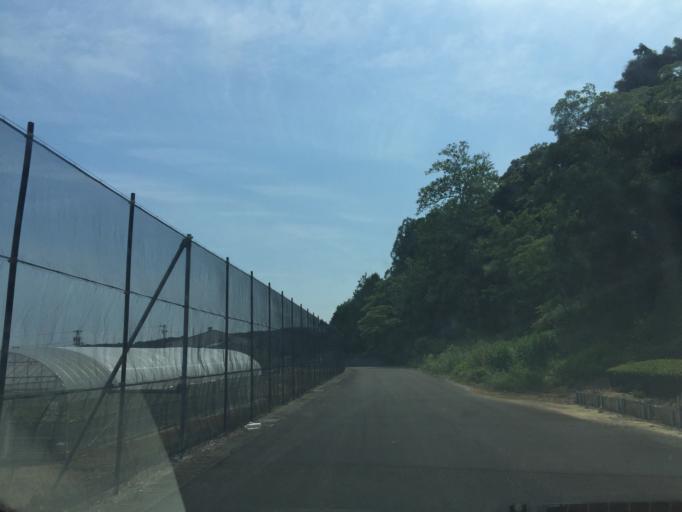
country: JP
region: Shizuoka
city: Mori
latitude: 34.8018
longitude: 137.9430
